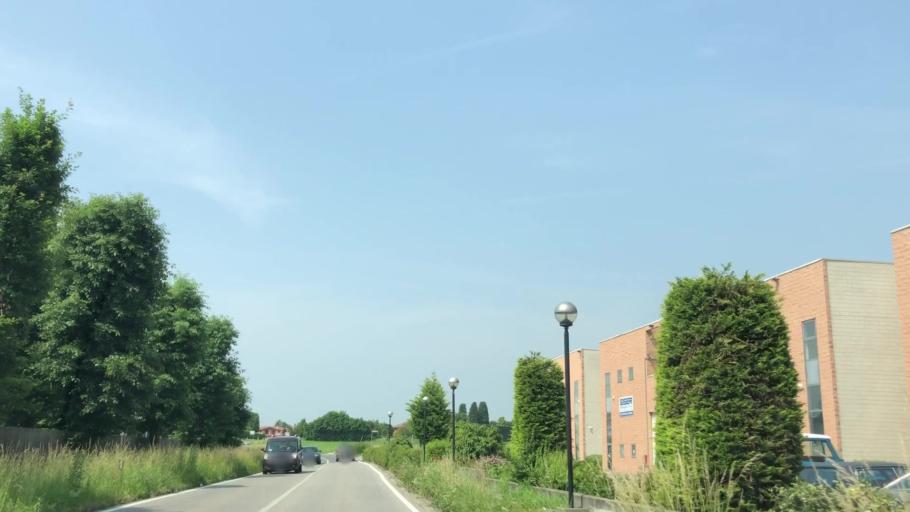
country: IT
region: Lombardy
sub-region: Provincia di Como
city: Vertemate Con Minoprio
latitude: 45.7253
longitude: 9.0647
